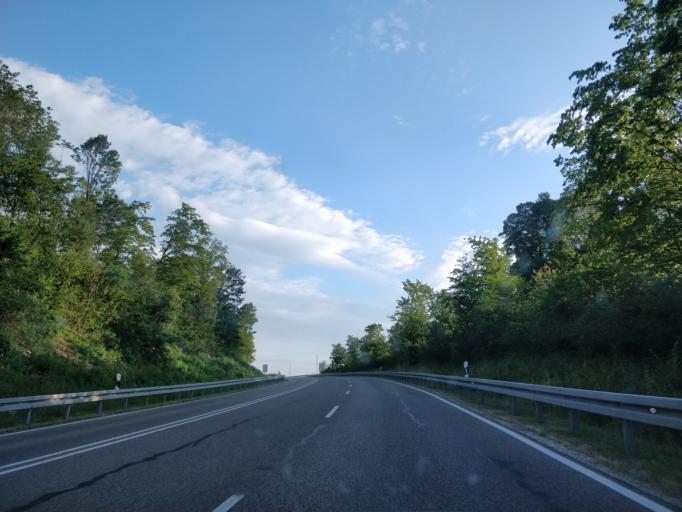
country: DE
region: Bavaria
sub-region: Swabia
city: Ederheim
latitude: 48.8193
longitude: 10.4580
